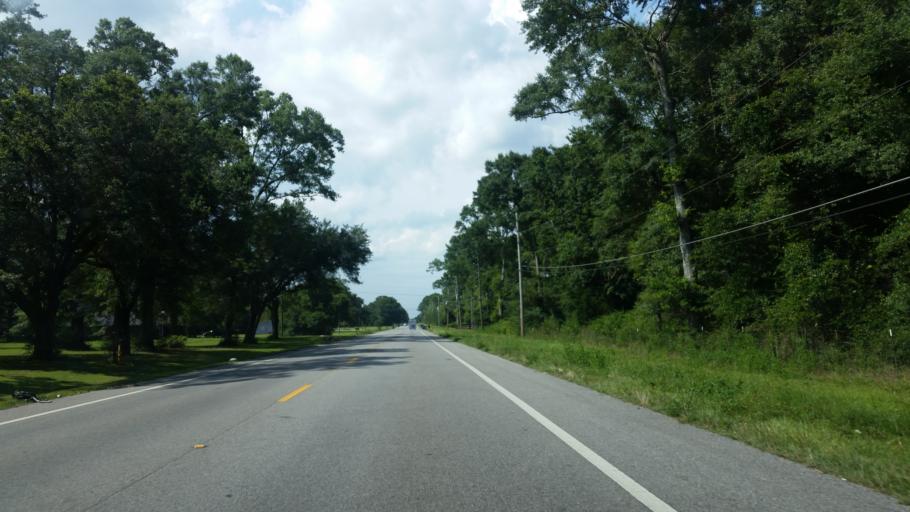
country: US
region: Florida
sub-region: Escambia County
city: Cantonment
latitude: 30.5811
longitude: -87.3494
